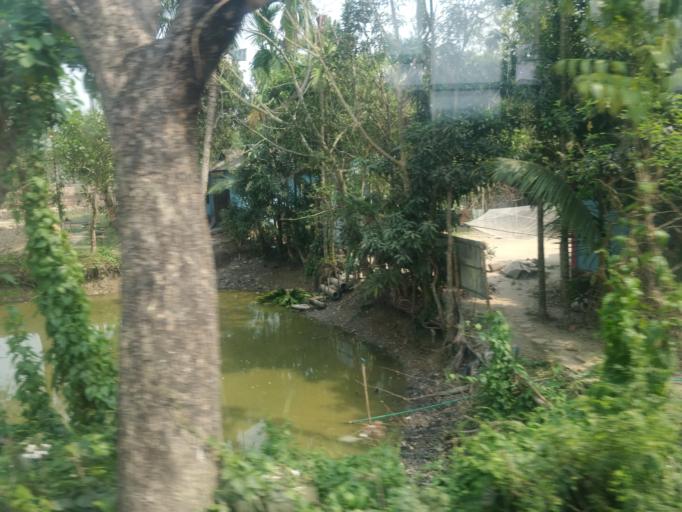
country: BD
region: Sylhet
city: Habiganj
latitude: 24.3137
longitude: 91.4361
